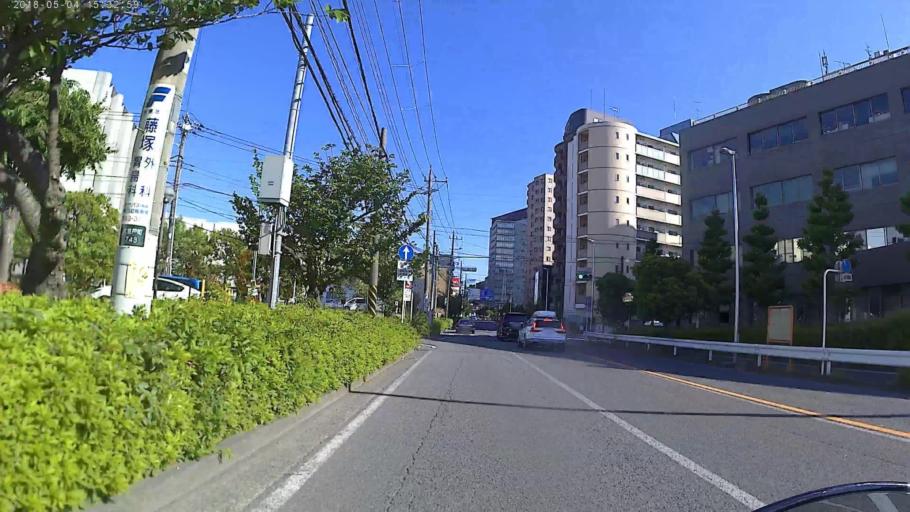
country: JP
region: Kanagawa
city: Yokohama
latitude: 35.5148
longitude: 139.6209
